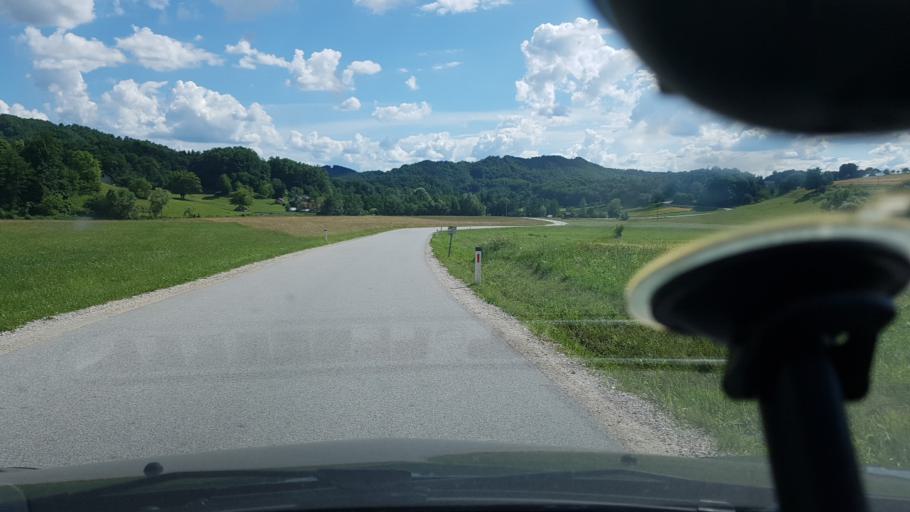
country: SI
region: Rogatec
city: Rogatec
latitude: 46.2509
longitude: 15.7308
